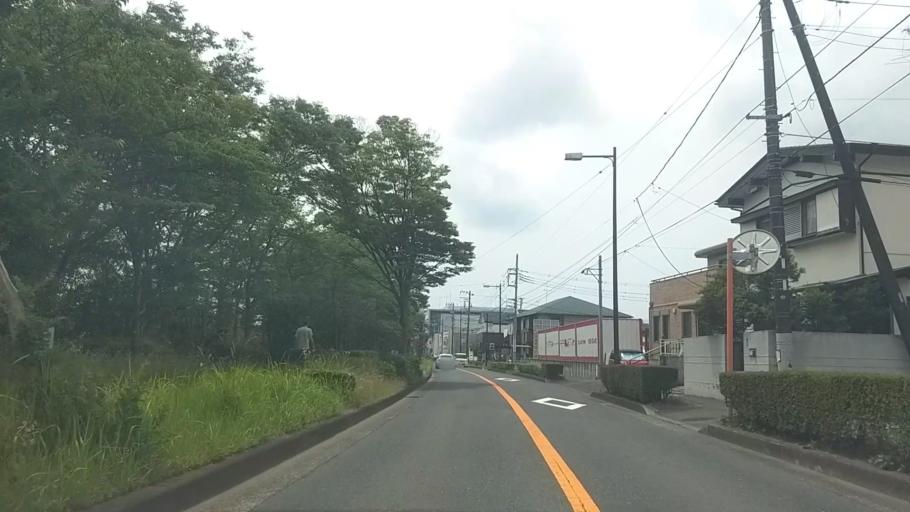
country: JP
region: Kanagawa
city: Fujisawa
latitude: 35.3453
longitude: 139.4666
